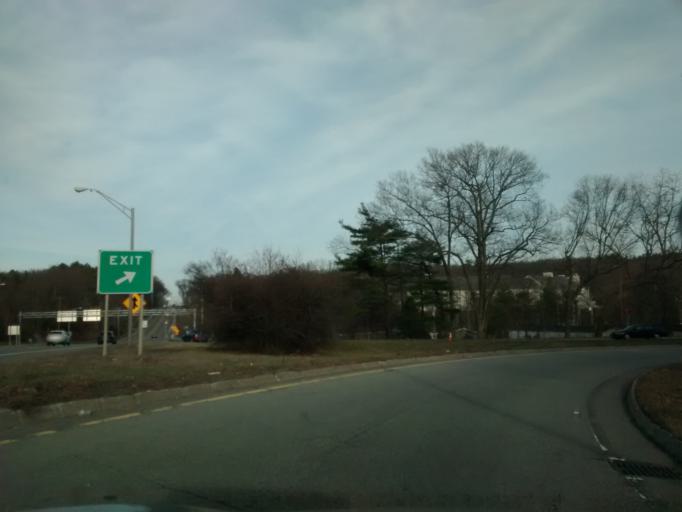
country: US
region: Massachusetts
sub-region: Worcester County
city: Auburn
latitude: 42.1843
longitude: -71.8457
